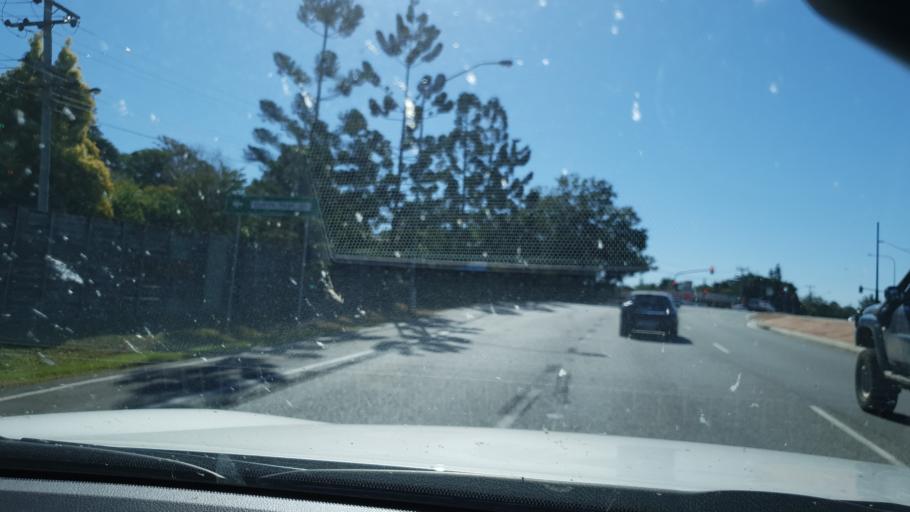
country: AU
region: Queensland
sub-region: Brisbane
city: Bridegman Downs
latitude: -27.3395
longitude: 152.9608
